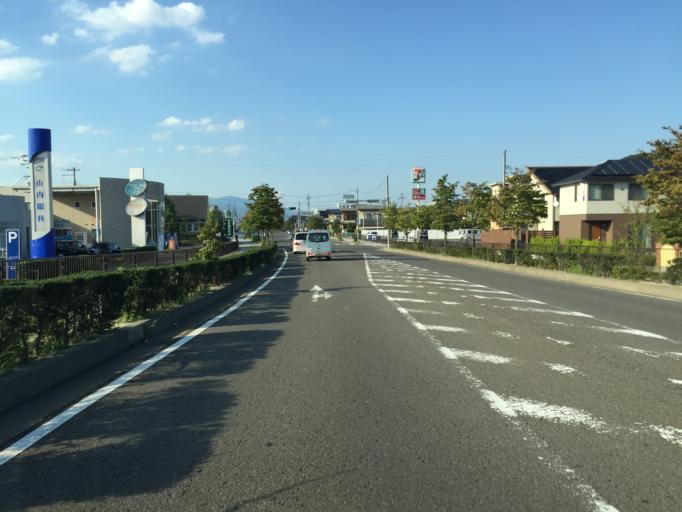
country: JP
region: Fukushima
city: Fukushima-shi
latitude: 37.7433
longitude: 140.4817
